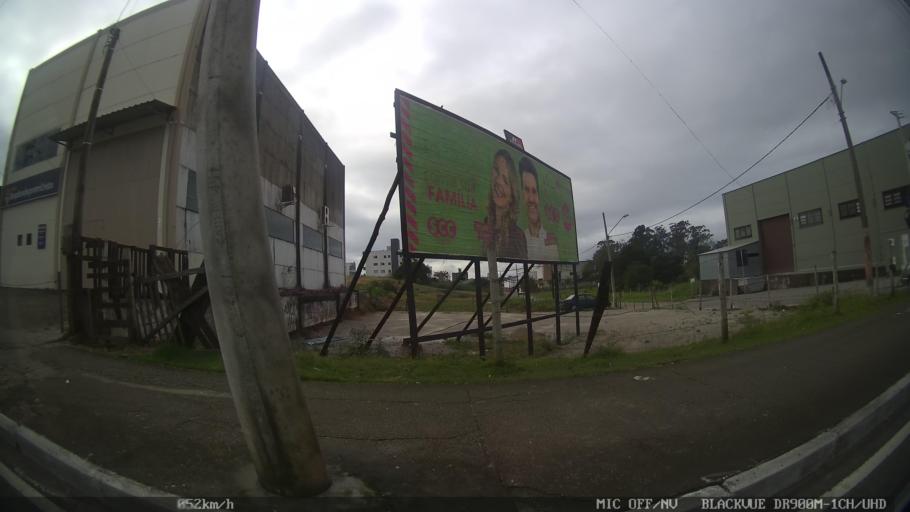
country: BR
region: Santa Catarina
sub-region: Sao Jose
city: Campinas
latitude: -27.5604
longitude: -48.6380
